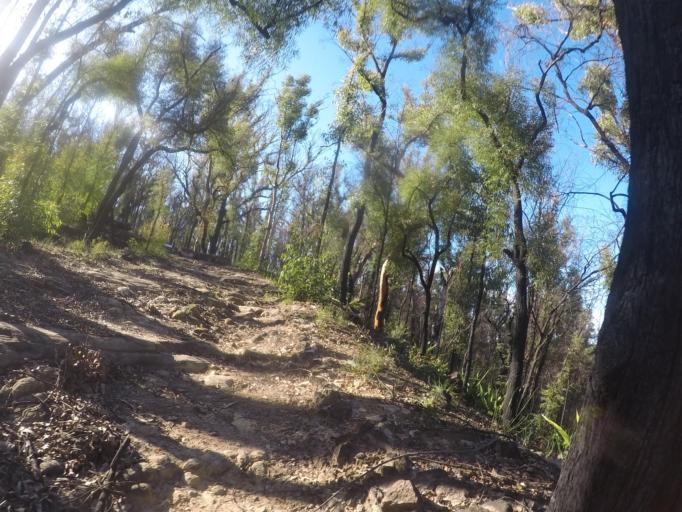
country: AU
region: New South Wales
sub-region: Hornsby Shire
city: Glenorie
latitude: -33.3500
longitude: 151.0346
